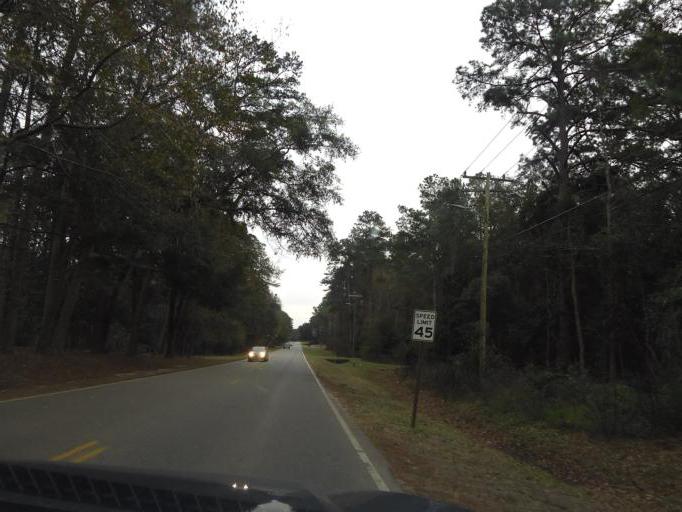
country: US
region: Georgia
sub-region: Thomas County
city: Thomasville
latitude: 30.8149
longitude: -83.9464
